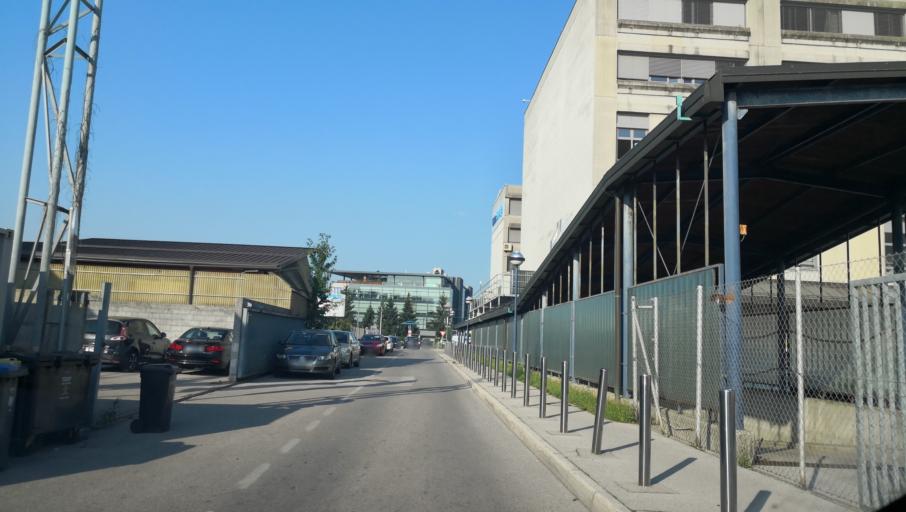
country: SI
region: Ljubljana
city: Ljubljana
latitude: 46.0857
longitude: 14.4835
